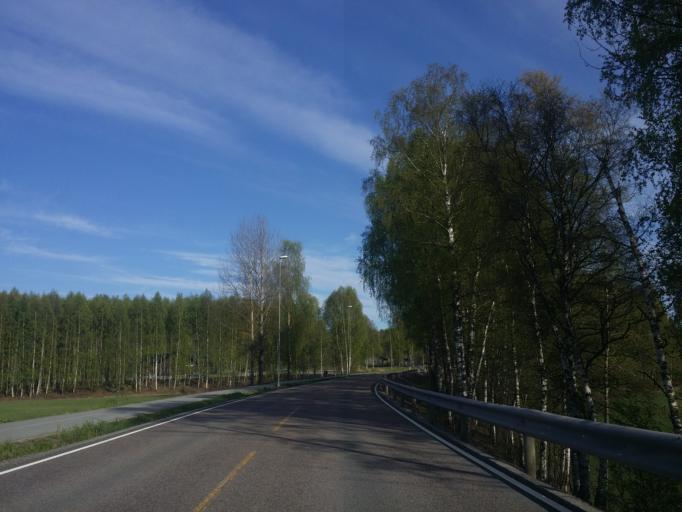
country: NO
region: Telemark
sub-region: Notodden
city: Notodden
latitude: 59.5920
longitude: 9.1495
